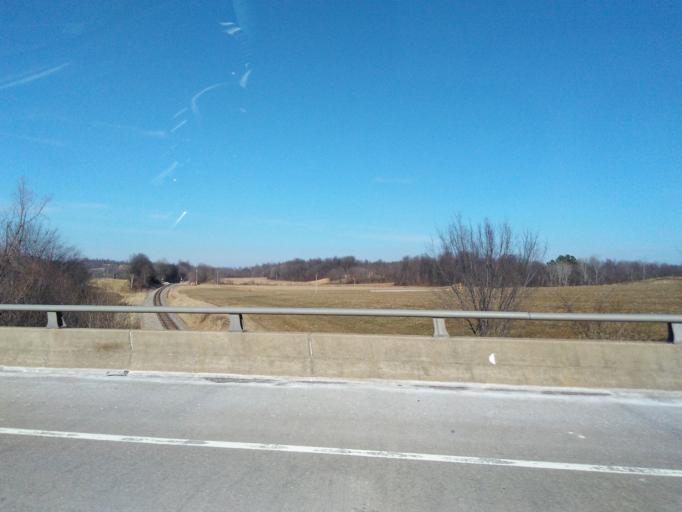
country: US
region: Illinois
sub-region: Massac County
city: Metropolis
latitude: 37.2690
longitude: -88.7398
